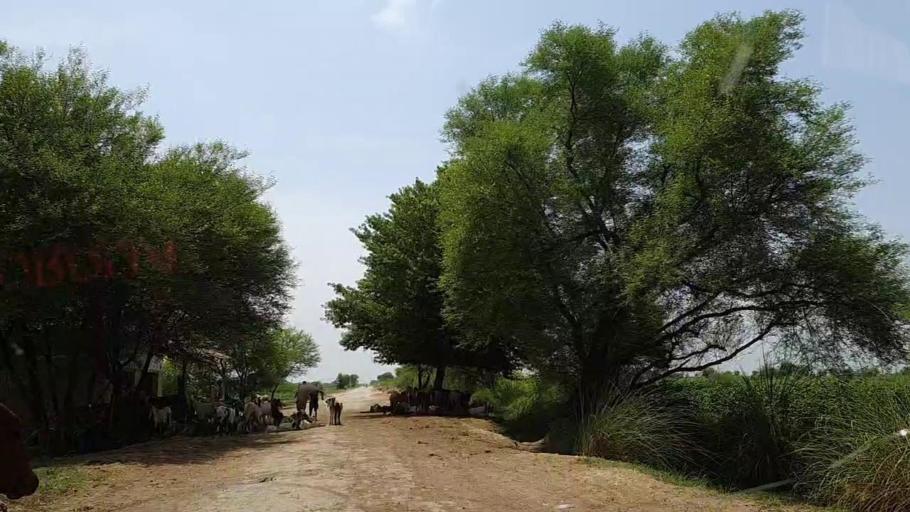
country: PK
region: Sindh
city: Khanpur
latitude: 27.8827
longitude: 69.4929
